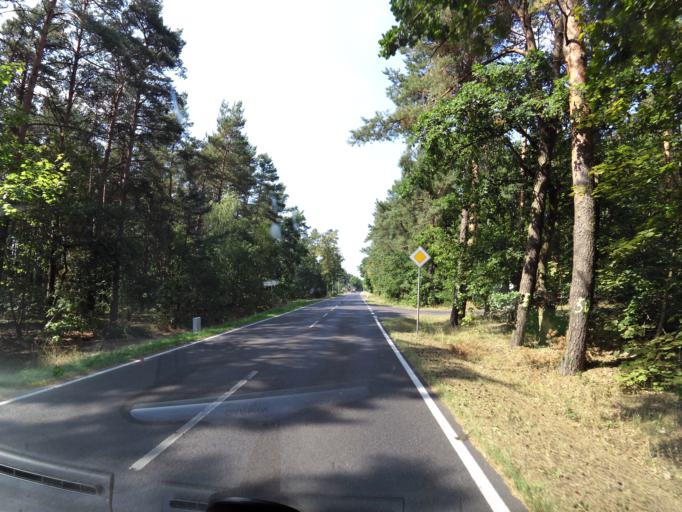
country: DE
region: Brandenburg
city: Zehdenick
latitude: 52.9654
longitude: 13.3646
